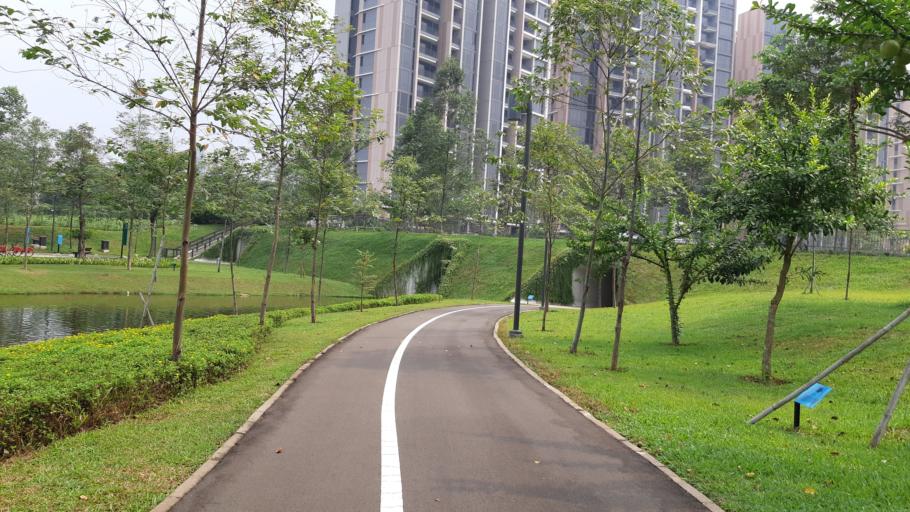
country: ID
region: West Java
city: Serpong
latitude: -6.2979
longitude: 106.6521
